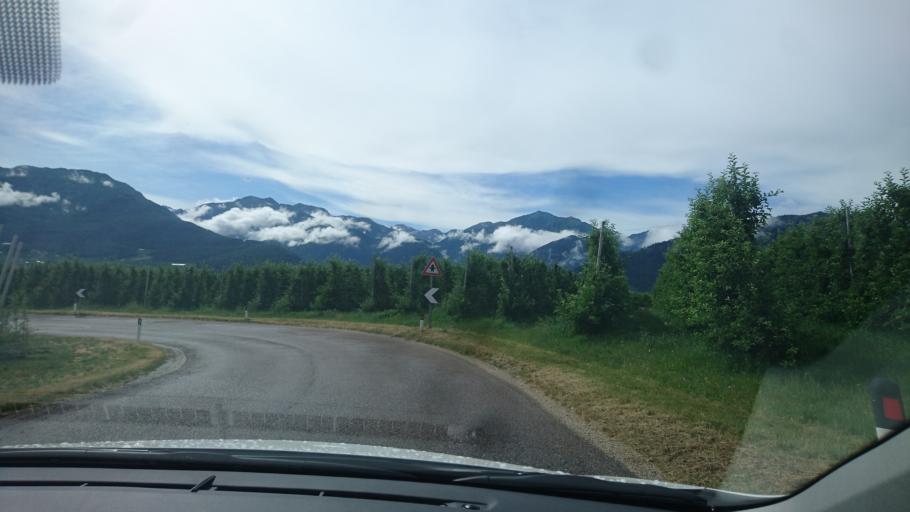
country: IT
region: Trentino-Alto Adige
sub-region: Provincia di Trento
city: Sanzeno
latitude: 46.3764
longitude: 11.0873
